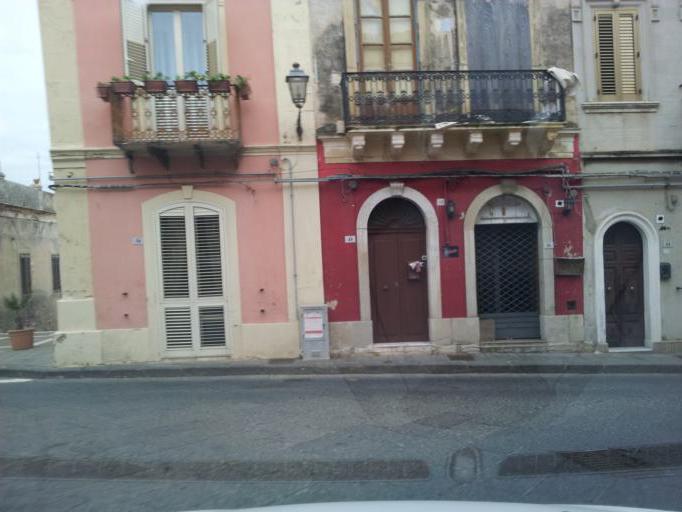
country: IT
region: Sicily
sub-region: Messina
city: Milazzo
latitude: 38.2303
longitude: 15.2434
